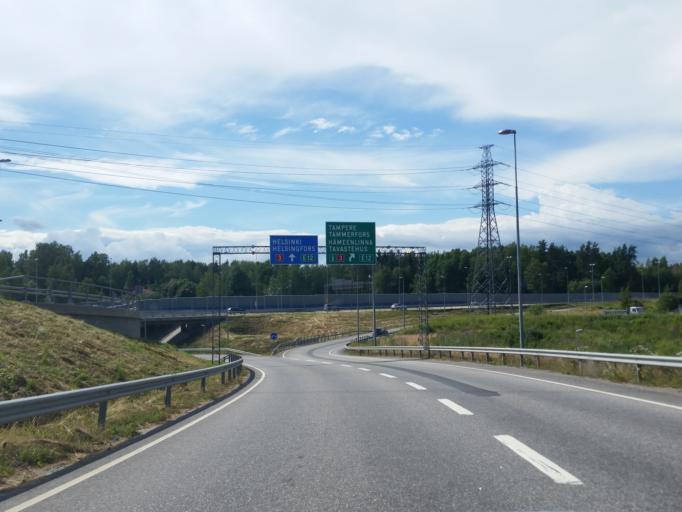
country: FI
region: Uusimaa
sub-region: Helsinki
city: Teekkarikylae
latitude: 60.2943
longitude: 24.8591
